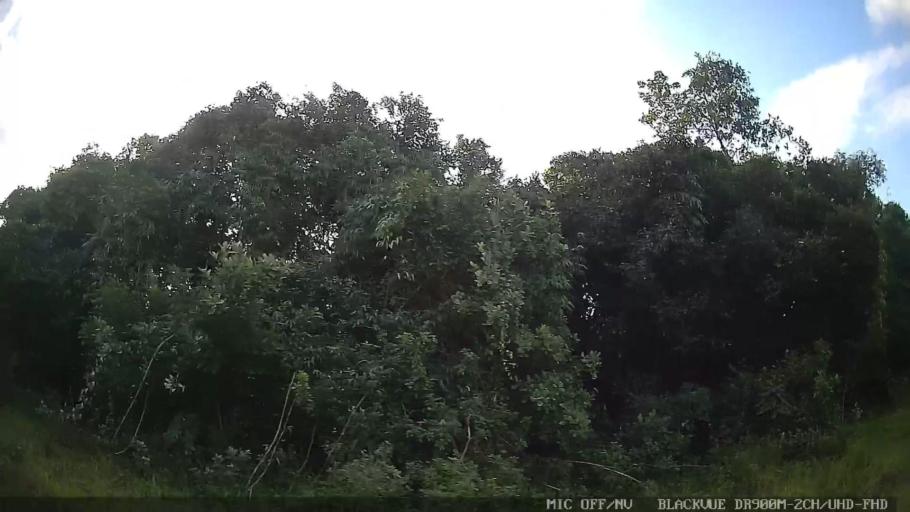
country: BR
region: Sao Paulo
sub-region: Itanhaem
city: Itanhaem
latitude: -24.1488
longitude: -46.8131
